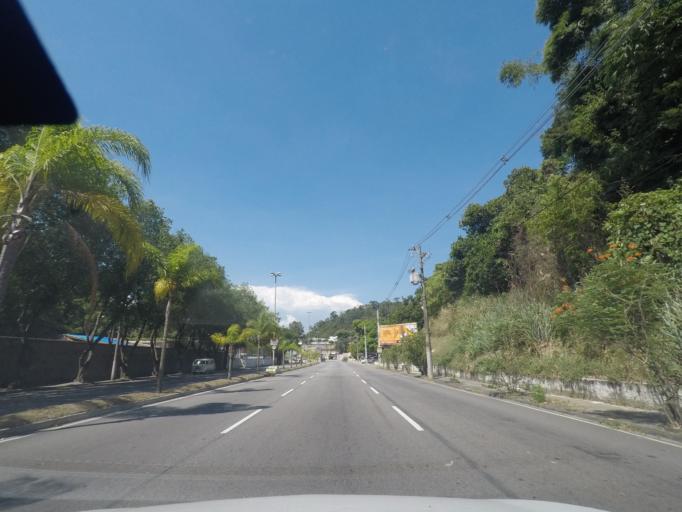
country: BR
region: Rio de Janeiro
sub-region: Niteroi
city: Niteroi
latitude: -22.9175
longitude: -43.0500
